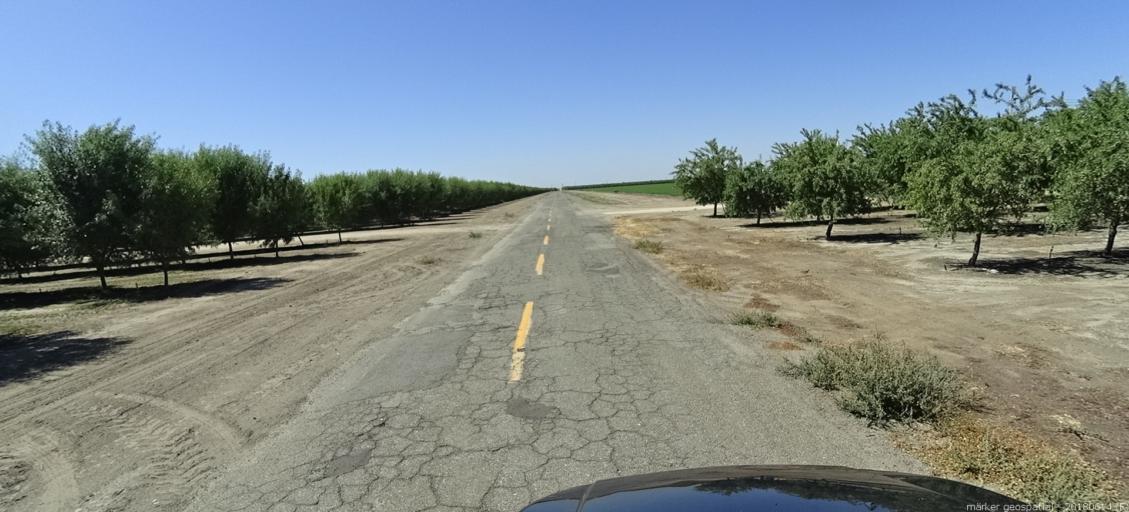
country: US
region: California
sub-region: Madera County
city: Fairmead
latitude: 36.9604
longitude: -120.2202
